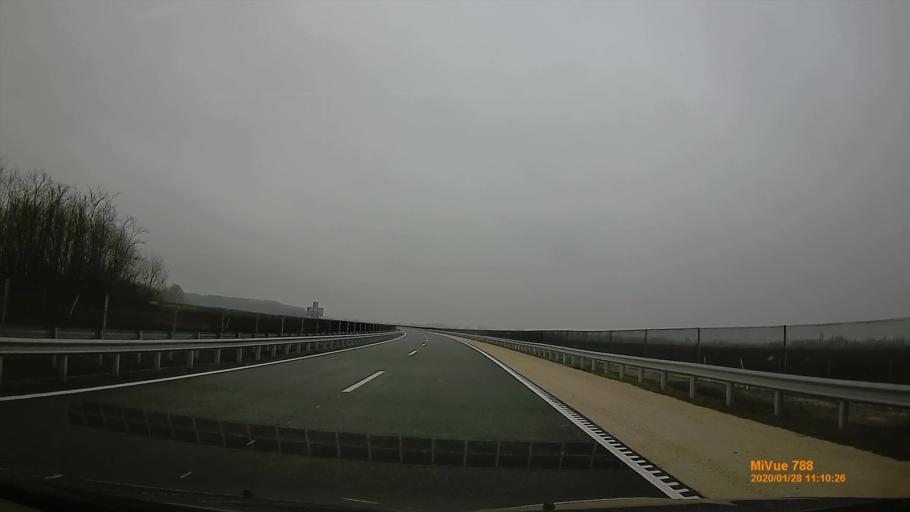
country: HU
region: Pest
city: Ullo
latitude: 47.3855
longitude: 19.3769
